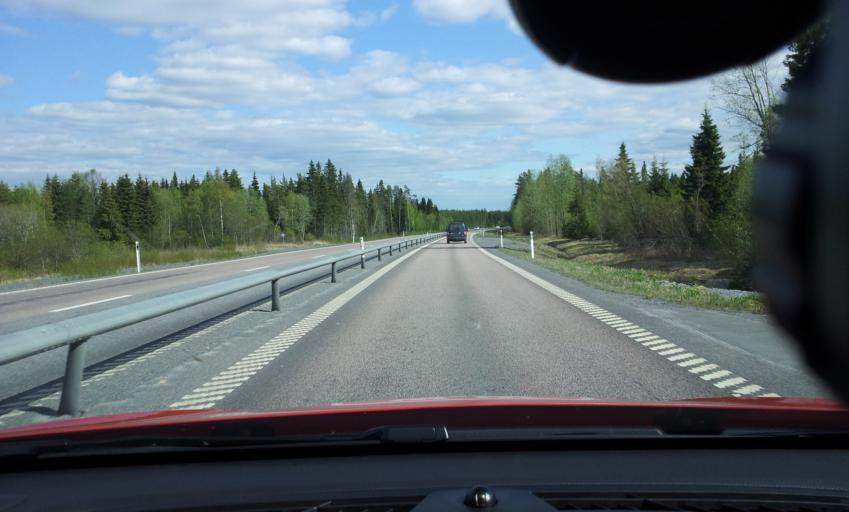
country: SE
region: Jaemtland
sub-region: OEstersunds Kommun
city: Ostersund
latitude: 63.2519
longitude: 14.5803
